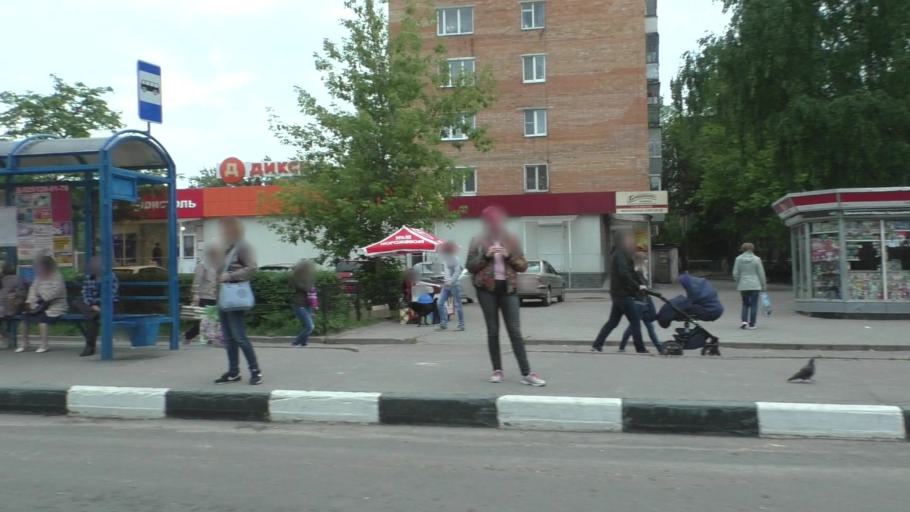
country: RU
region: Moskovskaya
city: Yegor'yevsk
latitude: 55.3692
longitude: 39.0656
